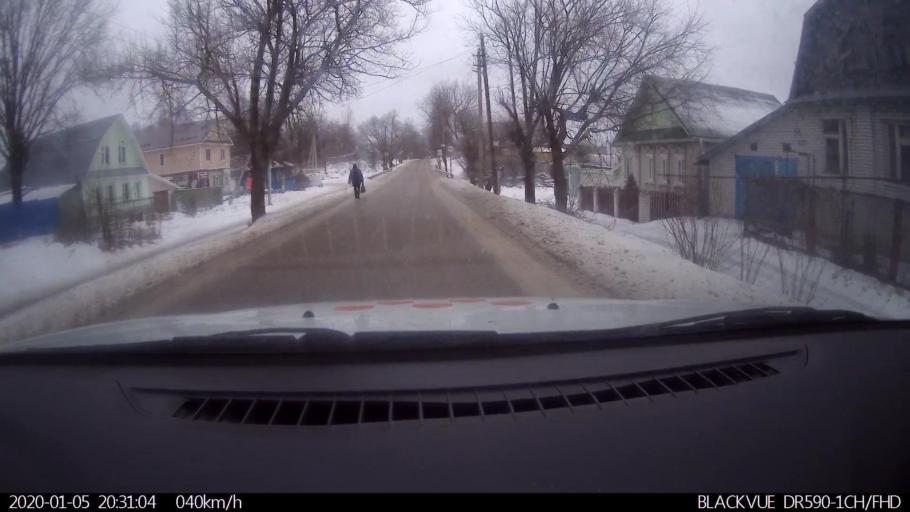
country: RU
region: Nizjnij Novgorod
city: Lukino
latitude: 56.4032
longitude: 43.7291
